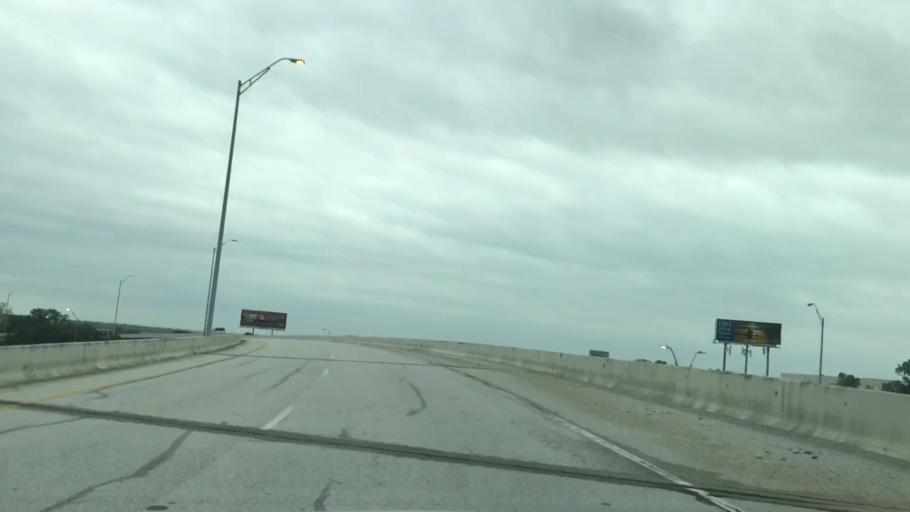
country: US
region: Texas
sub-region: Tarrant County
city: Euless
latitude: 32.8374
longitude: -97.0411
